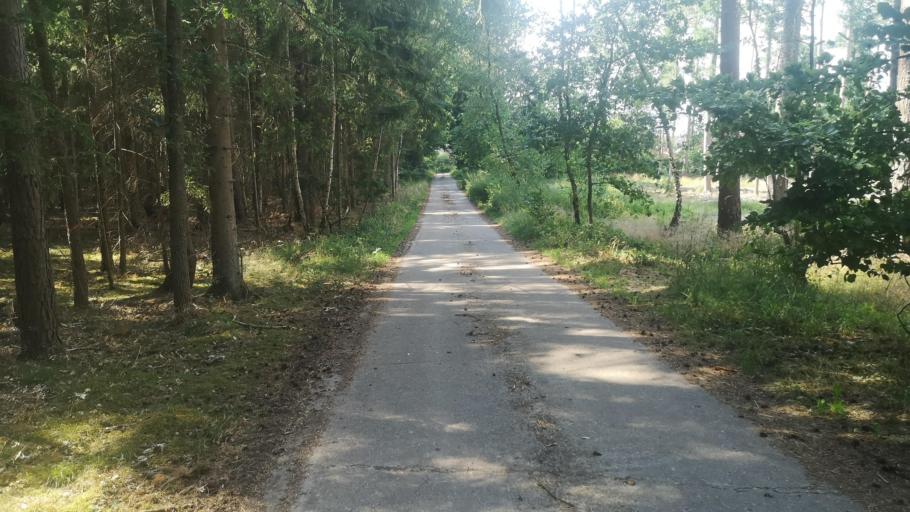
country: DE
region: Lower Saxony
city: Dahlem
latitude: 53.2175
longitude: 10.7296
